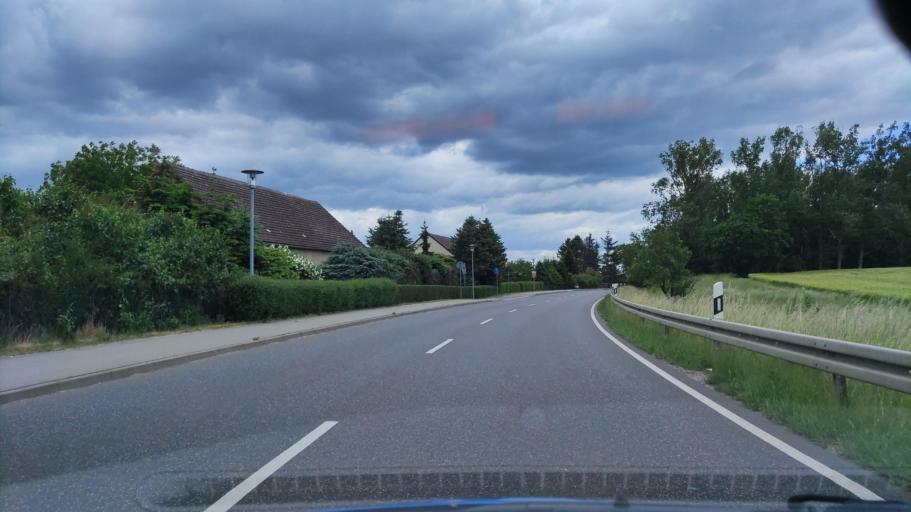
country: DE
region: Mecklenburg-Vorpommern
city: Spornitz
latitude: 53.4102
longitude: 11.7257
